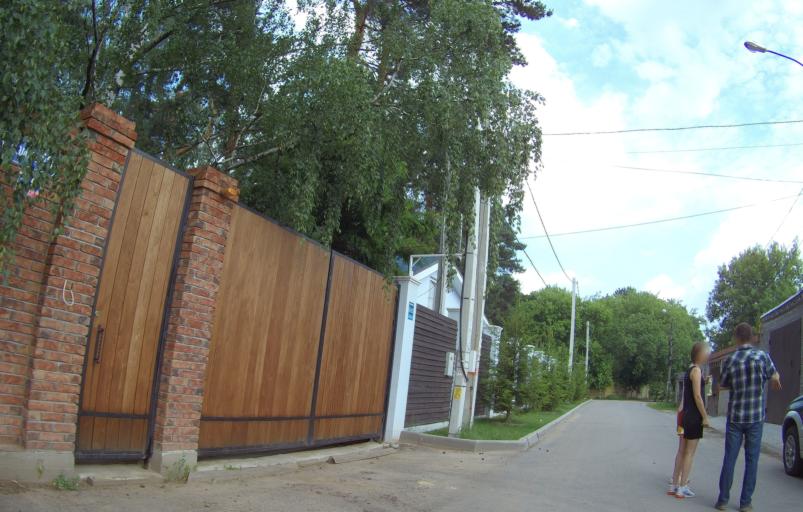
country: RU
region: Moskovskaya
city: Il'inskiy
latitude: 55.6097
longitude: 38.0992
